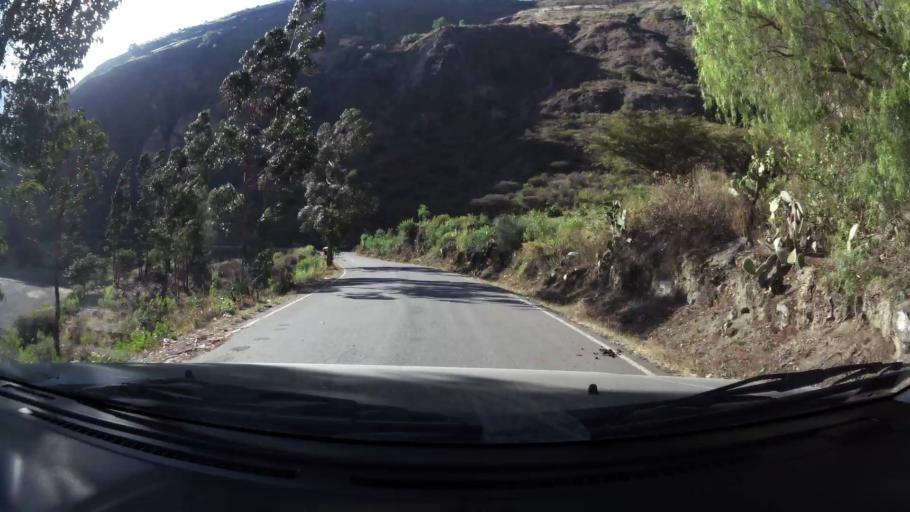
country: PE
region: Huancavelica
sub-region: Provincia de Churcampa
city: La Esmeralda
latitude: -12.5666
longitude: -74.6933
